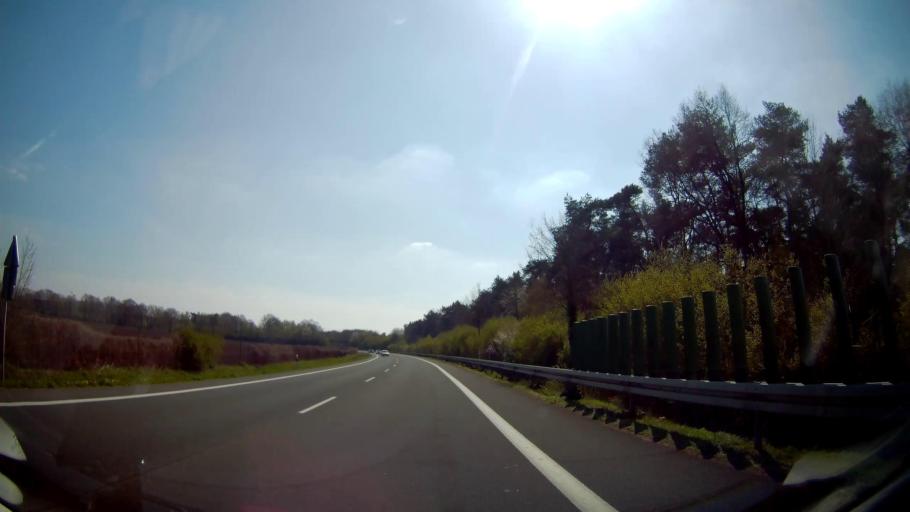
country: DE
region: North Rhine-Westphalia
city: Dorsten
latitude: 51.6934
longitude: 7.0105
